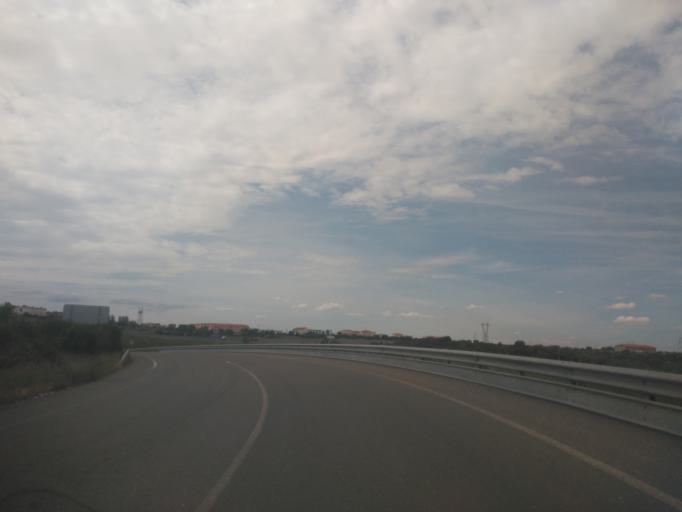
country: ES
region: Castille and Leon
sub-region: Provincia de Salamanca
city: Guijuelo
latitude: 40.5568
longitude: -5.6564
